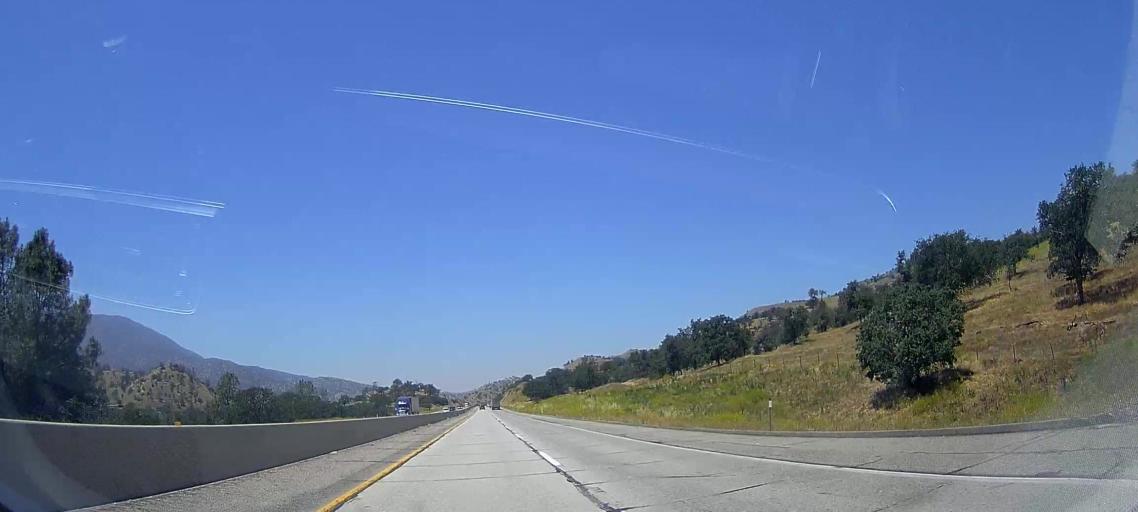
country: US
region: California
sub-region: Kern County
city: Golden Hills
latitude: 35.1913
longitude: -118.5083
